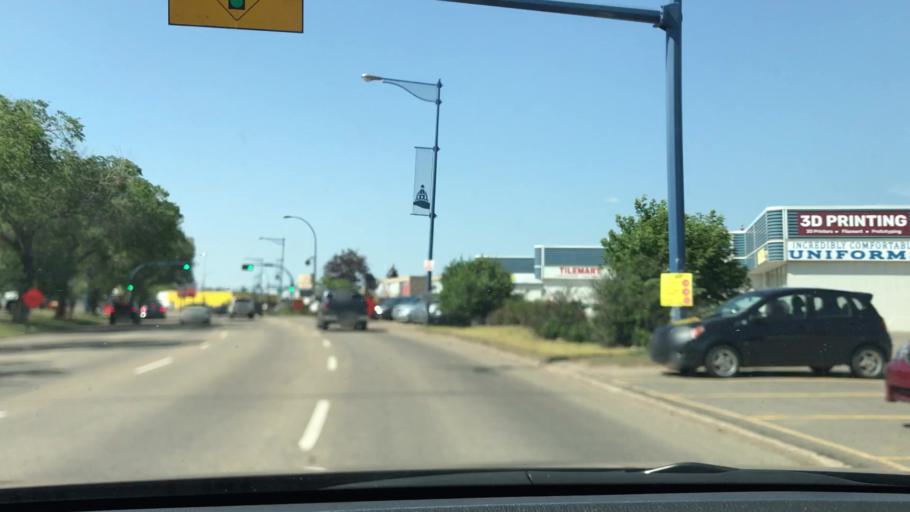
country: CA
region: Alberta
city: Edmonton
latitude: 53.4982
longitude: -113.4922
